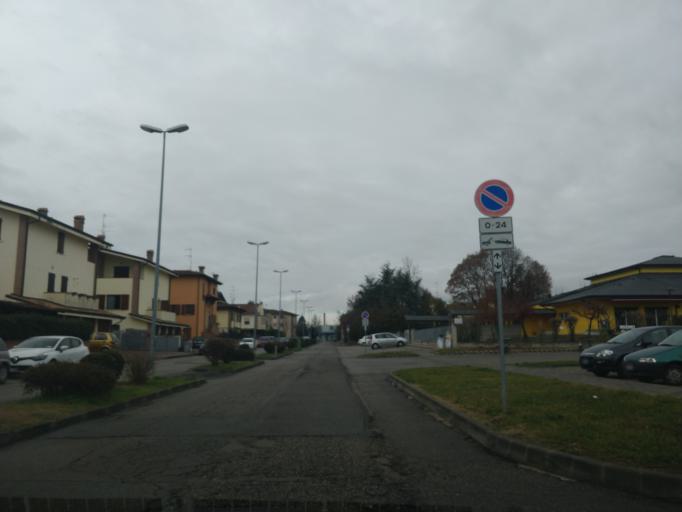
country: IT
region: Emilia-Romagna
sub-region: Provincia di Ferrara
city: Corpo Reno
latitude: 44.7542
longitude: 11.3109
